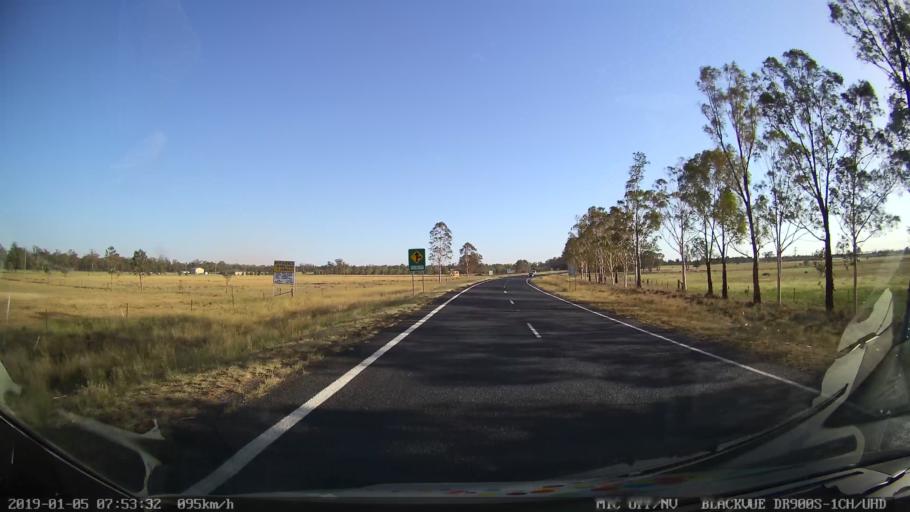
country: AU
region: New South Wales
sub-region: Gilgandra
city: Gilgandra
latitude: -31.7429
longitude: 148.6421
